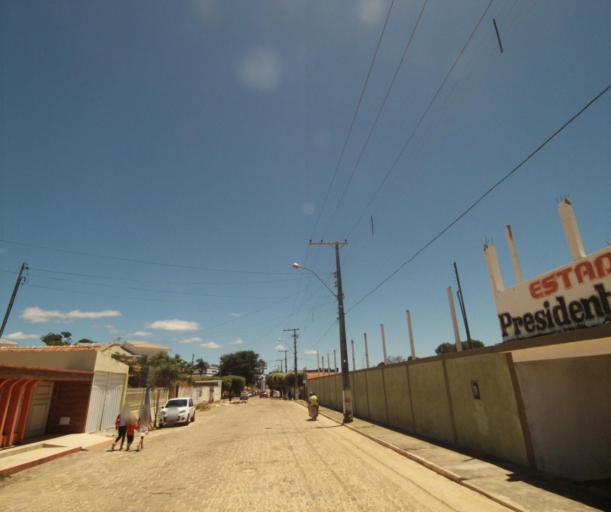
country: BR
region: Bahia
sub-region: Carinhanha
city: Carinhanha
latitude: -14.3071
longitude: -43.7689
